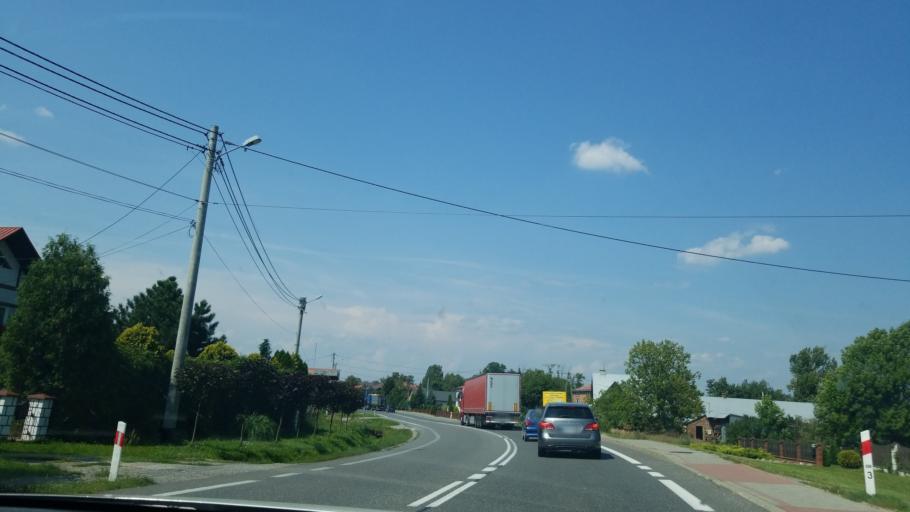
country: PL
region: Subcarpathian Voivodeship
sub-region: Powiat rzeszowski
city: Kamien
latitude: 50.3406
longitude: 22.1355
